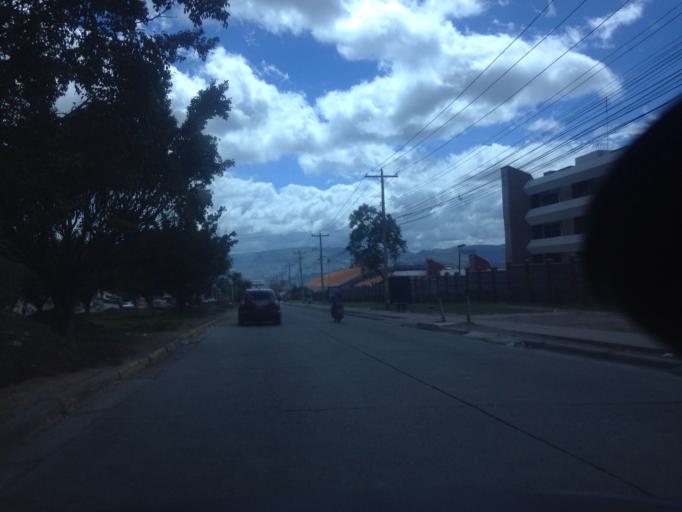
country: HN
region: Francisco Morazan
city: Tegucigalpa
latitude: 14.0833
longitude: -87.1662
